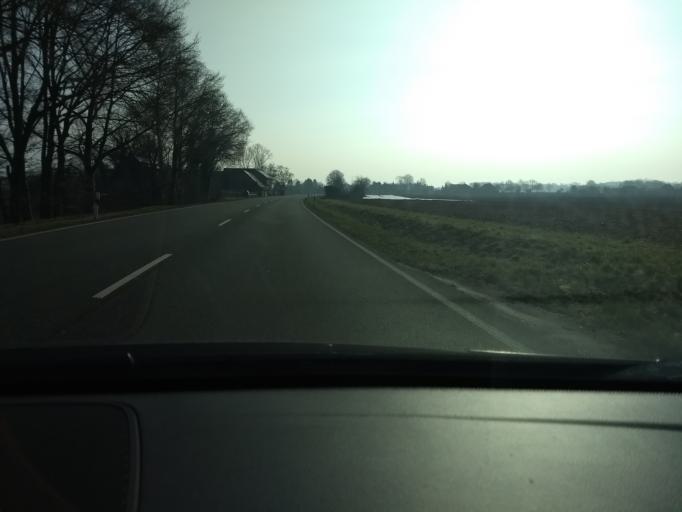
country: DE
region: North Rhine-Westphalia
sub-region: Regierungsbezirk Munster
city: Rhede
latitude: 51.8310
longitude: 6.7655
